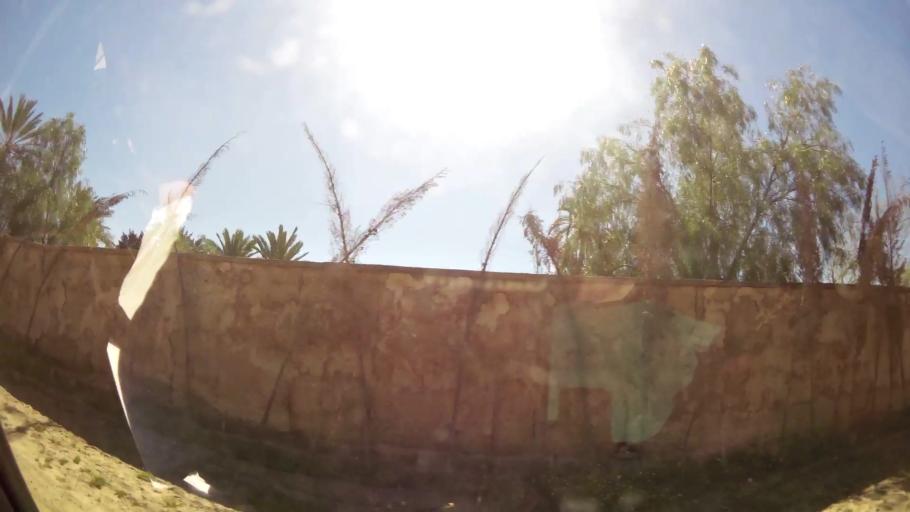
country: MA
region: Marrakech-Tensift-Al Haouz
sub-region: Marrakech
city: Marrakesh
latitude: 31.6701
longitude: -7.9600
